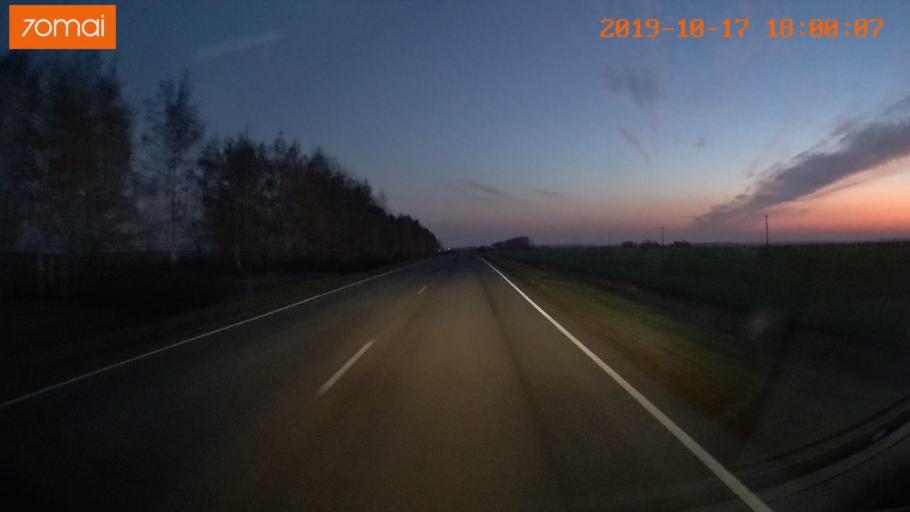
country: RU
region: Tula
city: Kurkino
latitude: 53.5258
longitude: 38.6172
